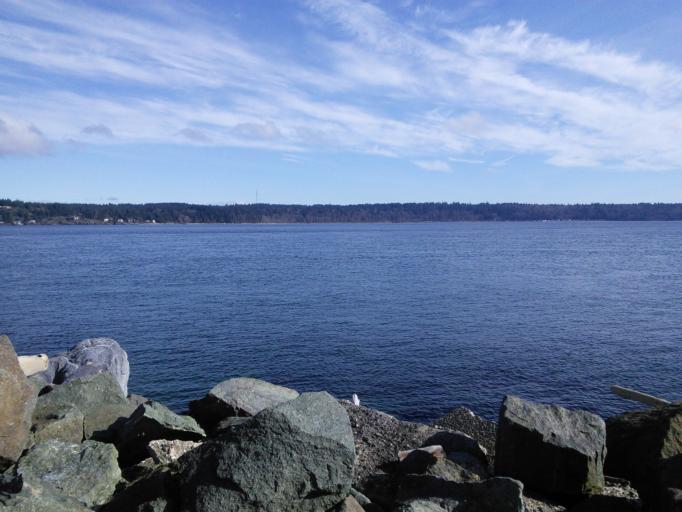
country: CA
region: British Columbia
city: Campbell River
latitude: 50.0270
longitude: -125.2403
